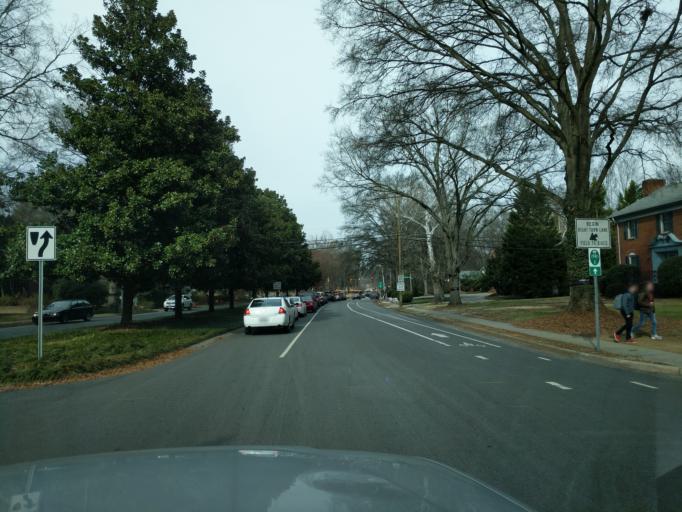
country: US
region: North Carolina
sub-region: Mecklenburg County
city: Charlotte
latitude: 35.1647
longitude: -80.8290
